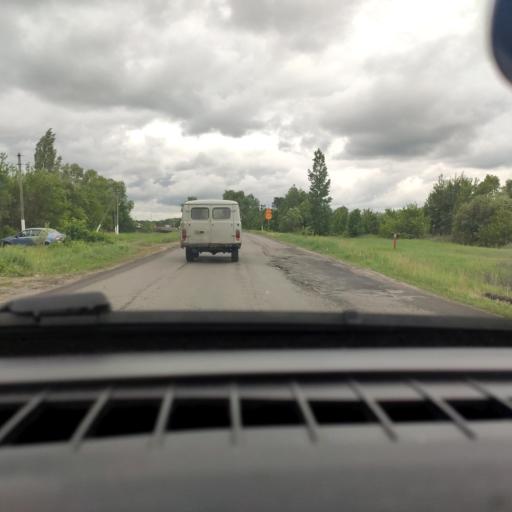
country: RU
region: Lipetsk
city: Usman'
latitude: 51.9447
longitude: 39.7808
